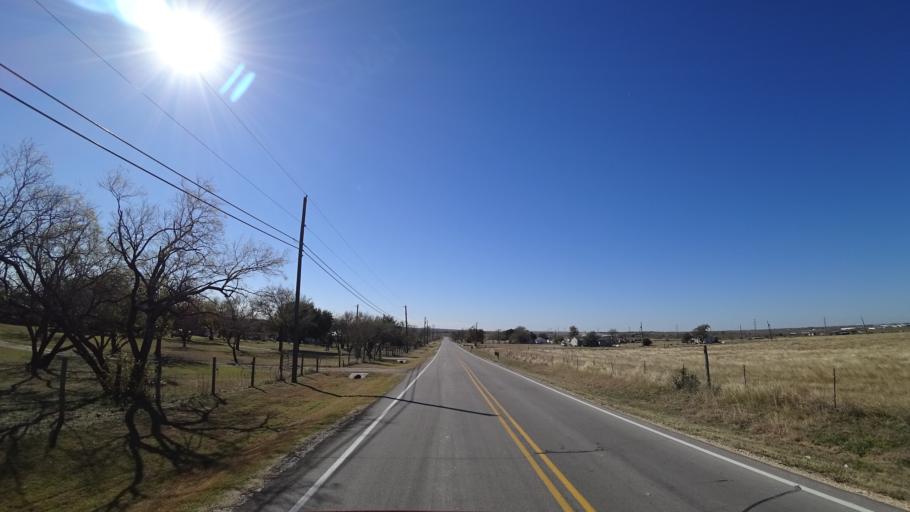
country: US
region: Texas
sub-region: Travis County
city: Garfield
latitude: 30.1191
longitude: -97.6459
